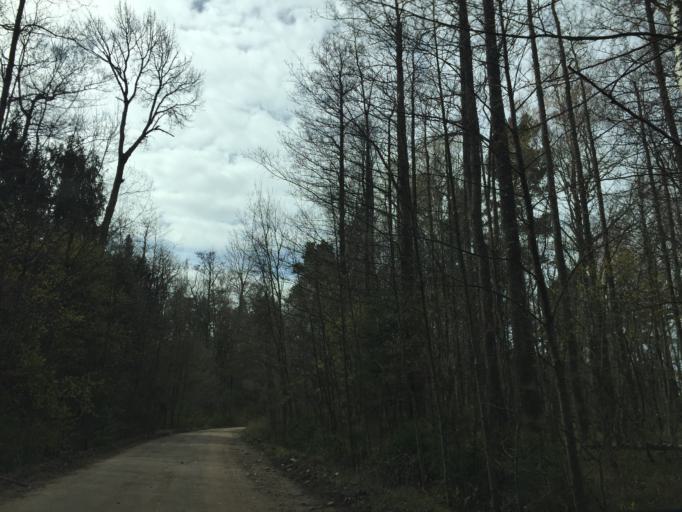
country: LV
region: Salacgrivas
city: Salacgriva
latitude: 57.5834
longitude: 24.3692
